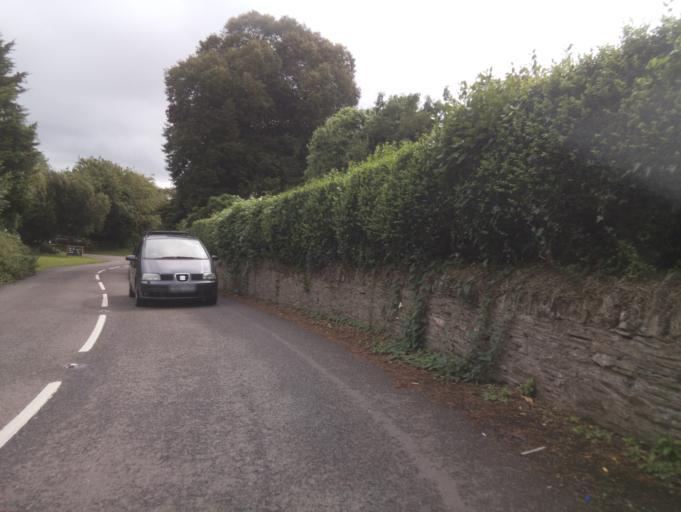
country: GB
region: England
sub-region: Devon
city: Salcombe
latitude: 50.2729
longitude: -3.6749
